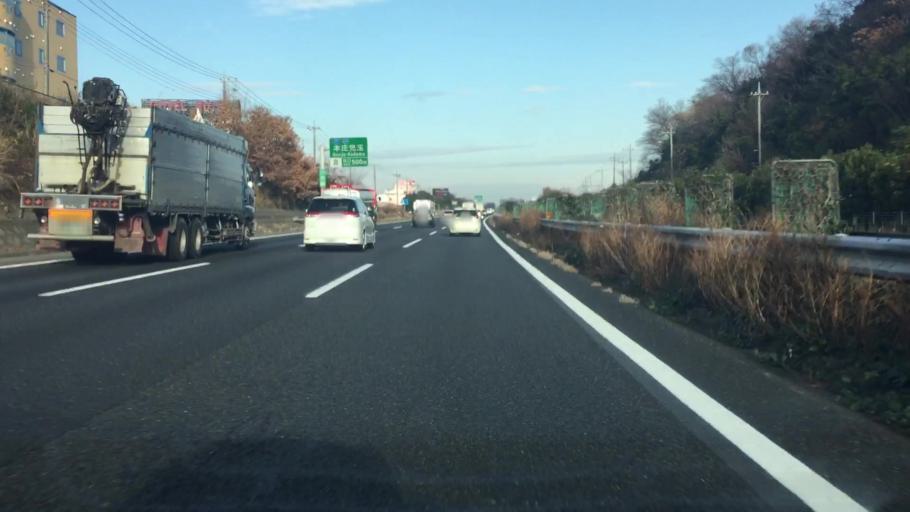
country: JP
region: Saitama
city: Honjo
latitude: 36.2116
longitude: 139.1690
